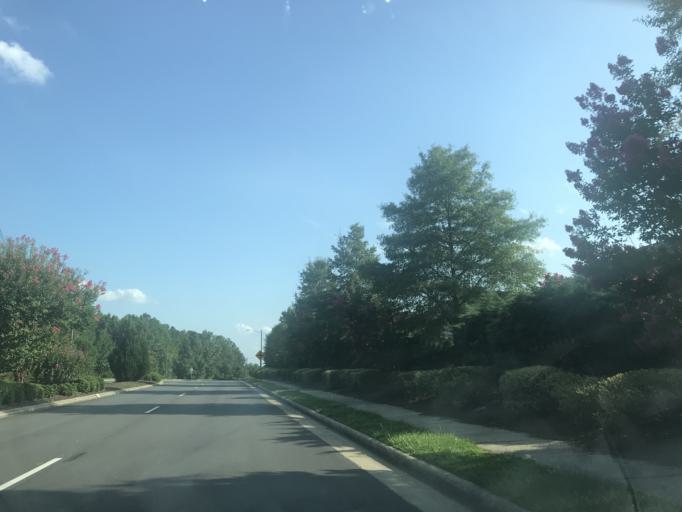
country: US
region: North Carolina
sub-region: Wake County
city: Knightdale
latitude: 35.7794
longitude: -78.5452
